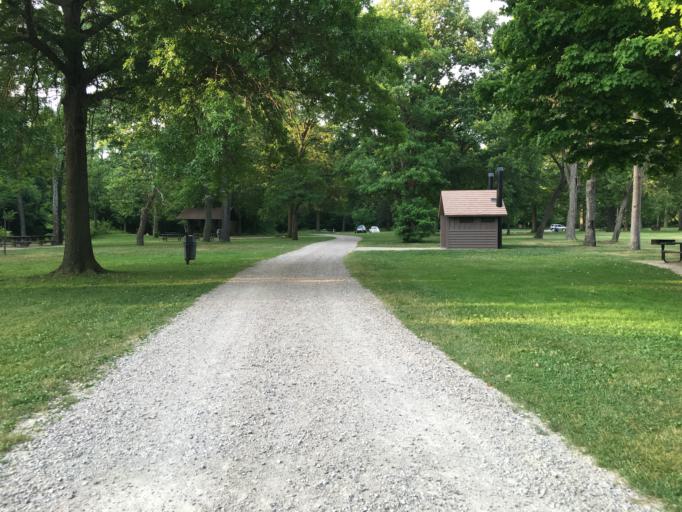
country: US
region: Ohio
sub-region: Cuyahoga County
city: Berea
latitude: 41.3632
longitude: -81.8585
